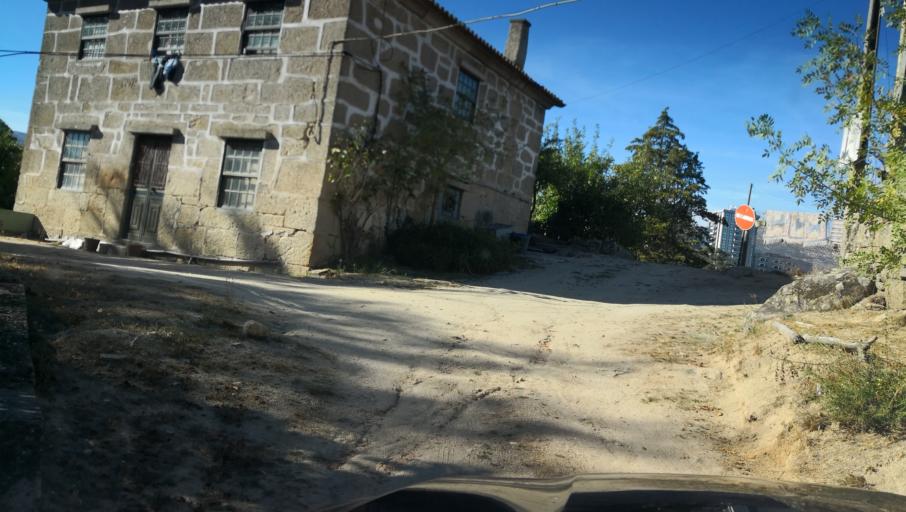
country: PT
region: Vila Real
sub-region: Vila Real
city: Vila Real
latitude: 41.2916
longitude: -7.7420
